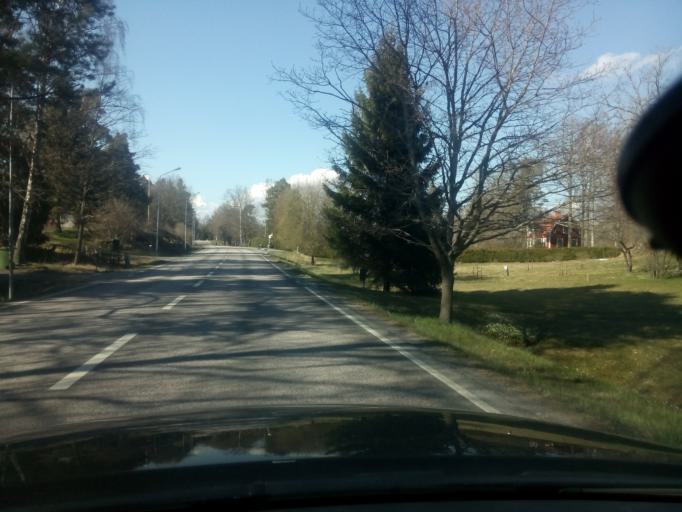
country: SE
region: Soedermanland
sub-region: Flens Kommun
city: Malmkoping
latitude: 59.0722
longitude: 16.8171
